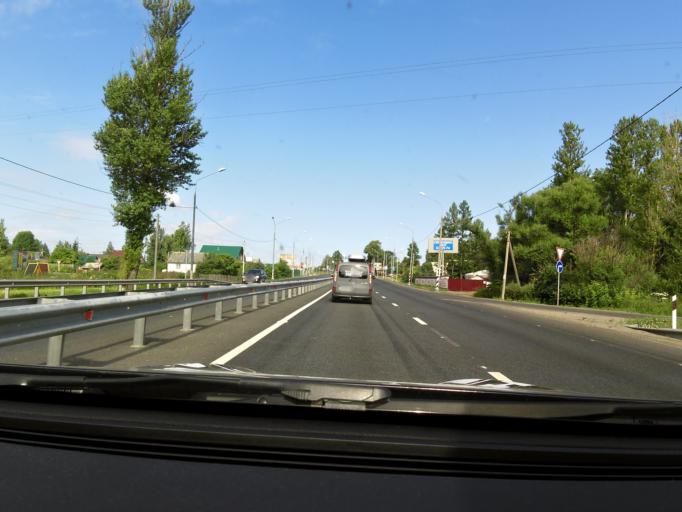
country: RU
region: Tverskaya
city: Emmaus
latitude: 56.7778
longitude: 36.1157
